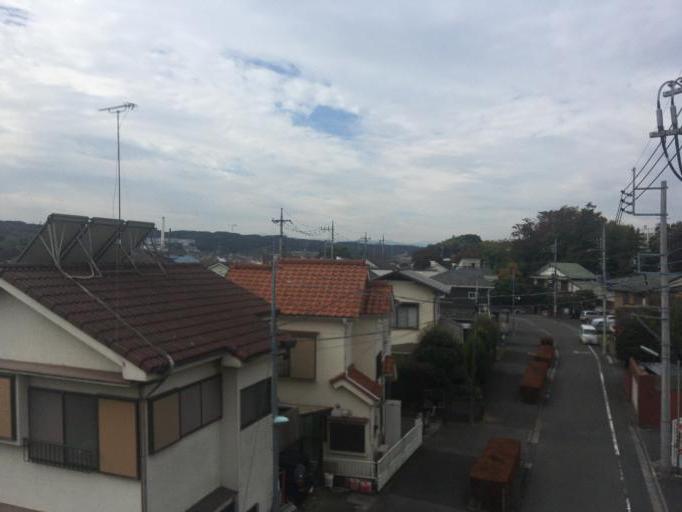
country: JP
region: Tokyo
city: Hino
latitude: 35.6979
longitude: 139.3632
